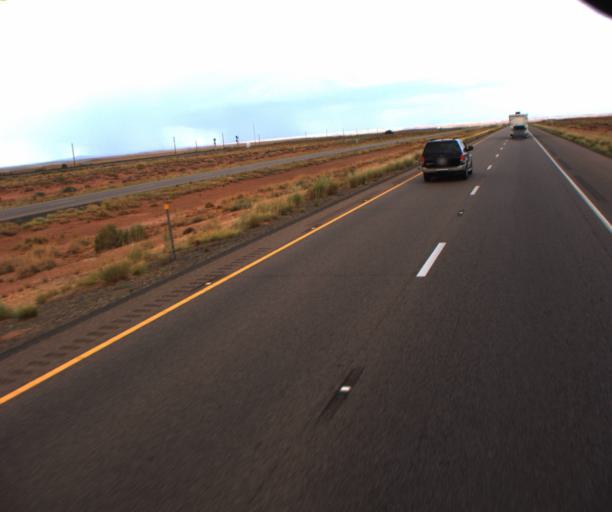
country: US
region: Arizona
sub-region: Coconino County
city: LeChee
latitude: 35.0838
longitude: -110.8899
